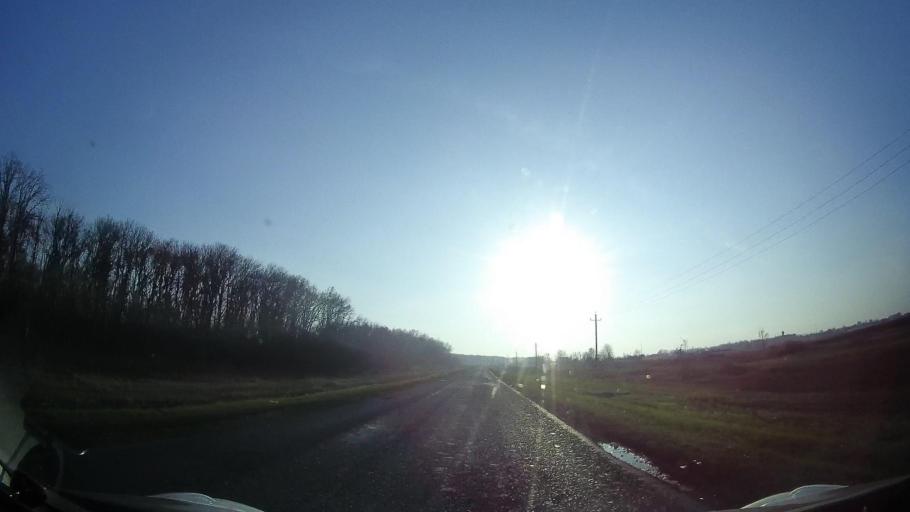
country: RU
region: Rostov
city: Ol'ginskaya
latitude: 47.1412
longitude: 39.9002
